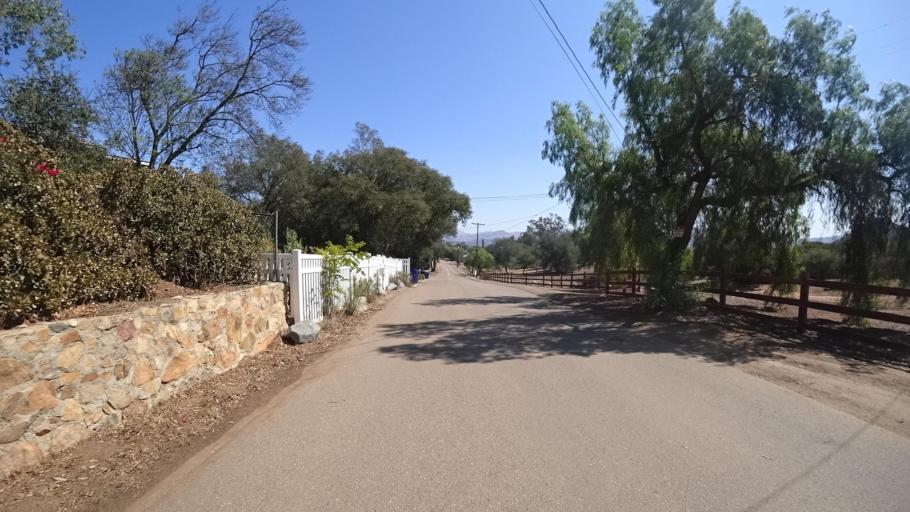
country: US
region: California
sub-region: San Diego County
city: Crest
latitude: 32.8010
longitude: -116.8684
